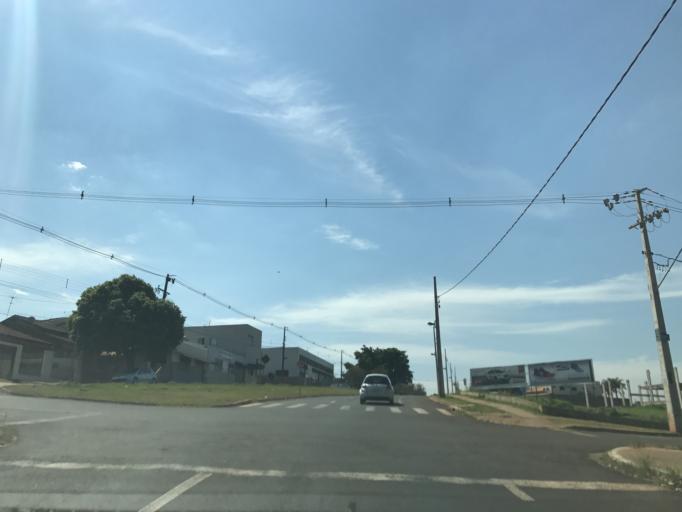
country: BR
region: Parana
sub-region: Maringa
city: Maringa
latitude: -23.4407
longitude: -51.9455
